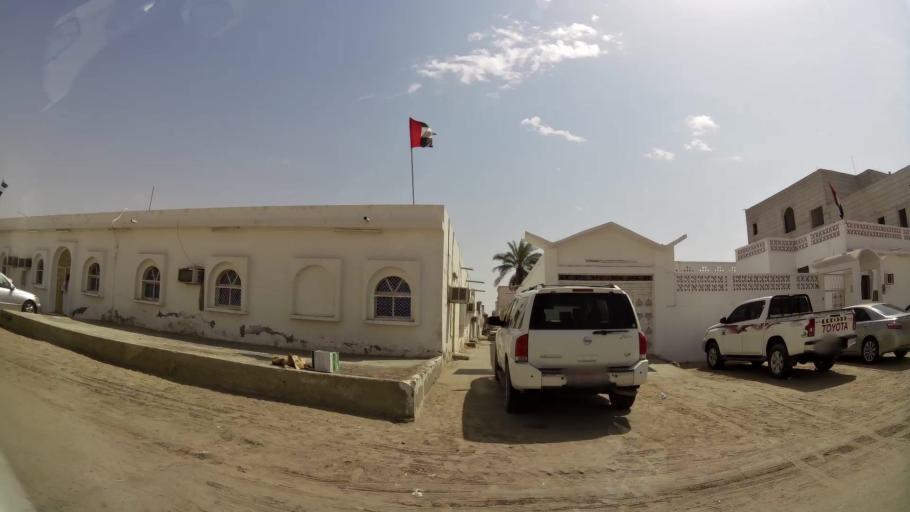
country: AE
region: Abu Dhabi
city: Abu Dhabi
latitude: 24.2999
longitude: 54.6386
